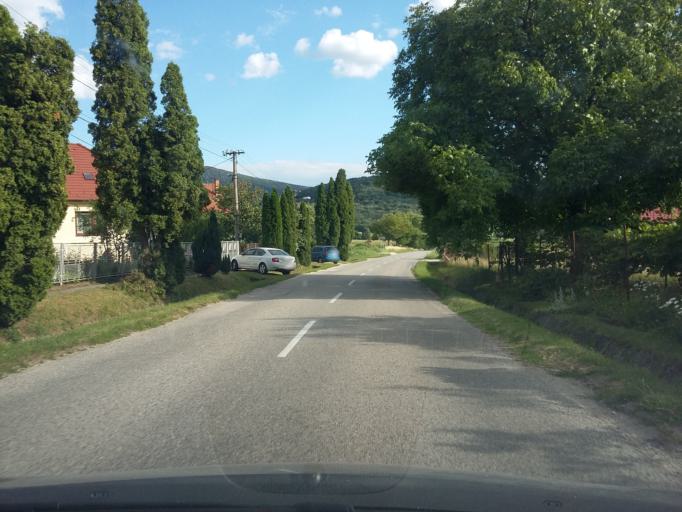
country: SK
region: Trnavsky
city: Smolenice
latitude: 48.5527
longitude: 17.3498
